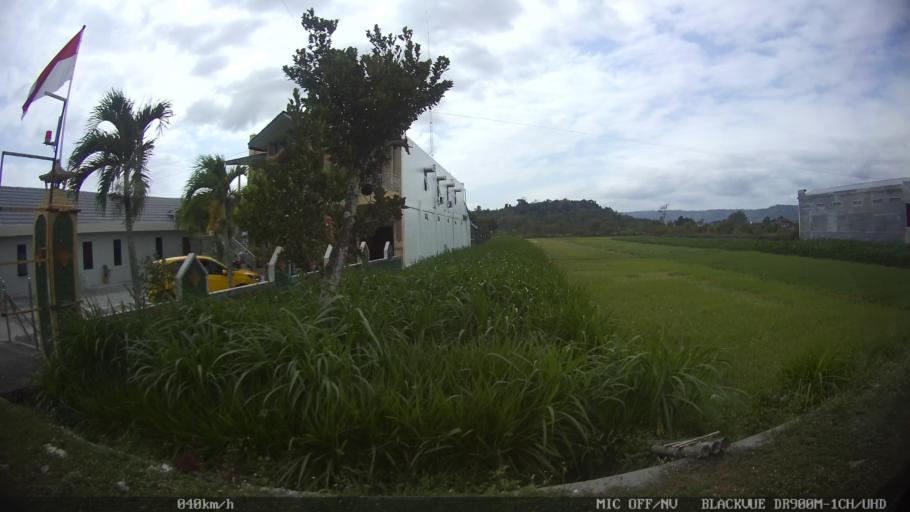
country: ID
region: Daerah Istimewa Yogyakarta
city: Depok
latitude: -7.8087
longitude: 110.4621
